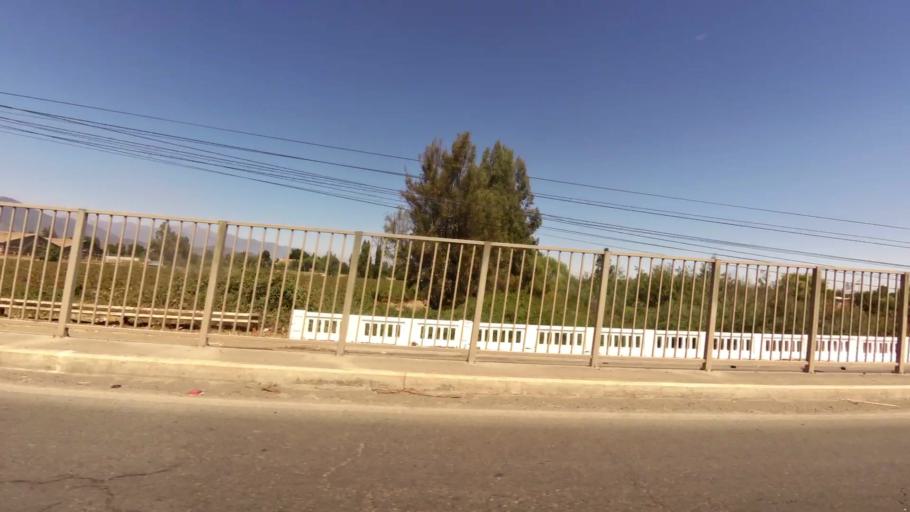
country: CL
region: O'Higgins
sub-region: Provincia de Colchagua
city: Chimbarongo
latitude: -34.5799
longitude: -70.9784
